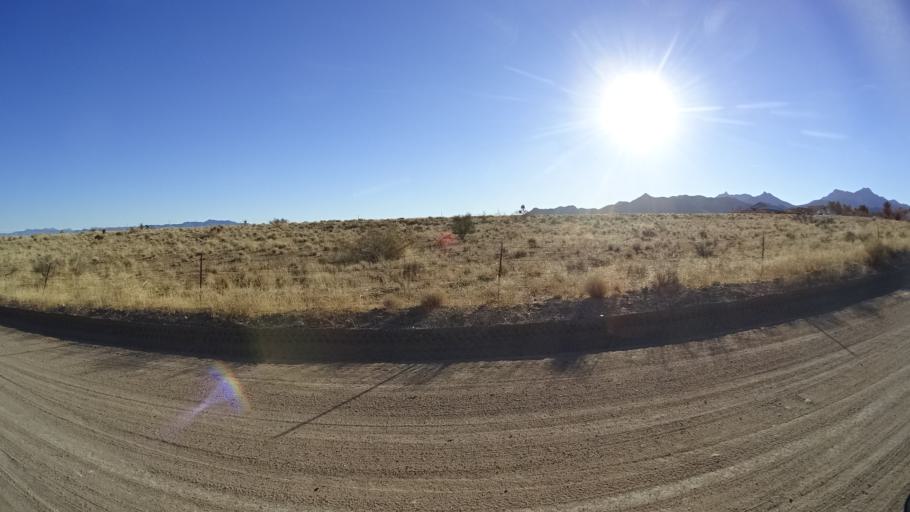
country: US
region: Arizona
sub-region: Mohave County
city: Kingman
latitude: 35.1971
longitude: -113.9939
